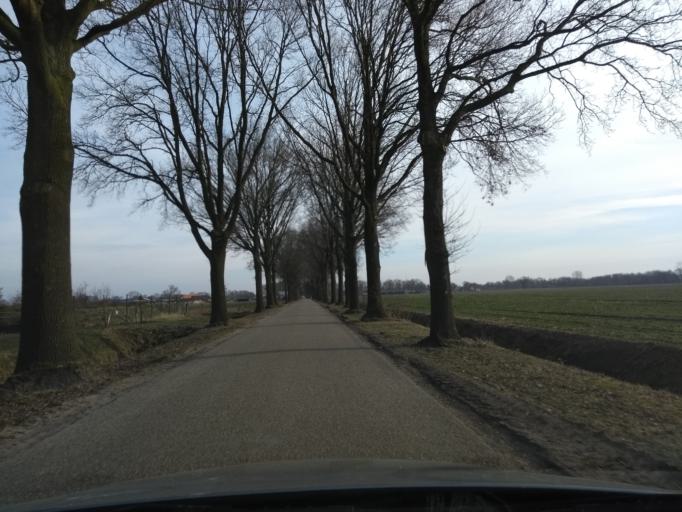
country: NL
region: Overijssel
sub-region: Gemeente Almelo
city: Almelo
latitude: 52.3929
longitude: 6.6811
